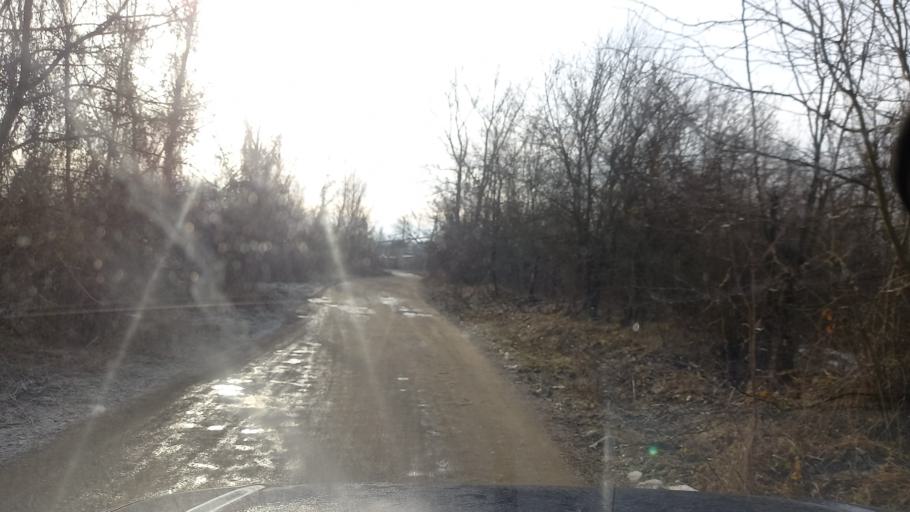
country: RU
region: Krasnodarskiy
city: Apsheronsk
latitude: 44.4847
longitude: 39.7314
